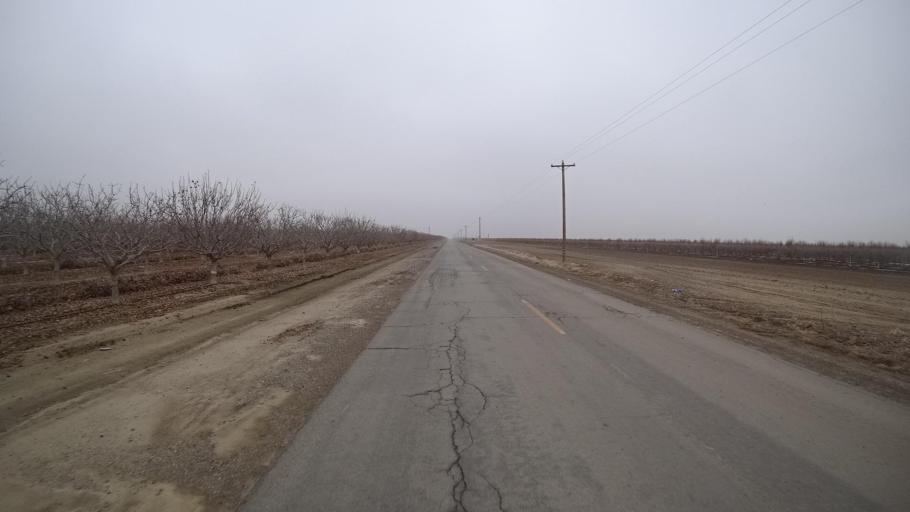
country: US
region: California
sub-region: Kern County
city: Wasco
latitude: 35.6479
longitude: -119.5088
